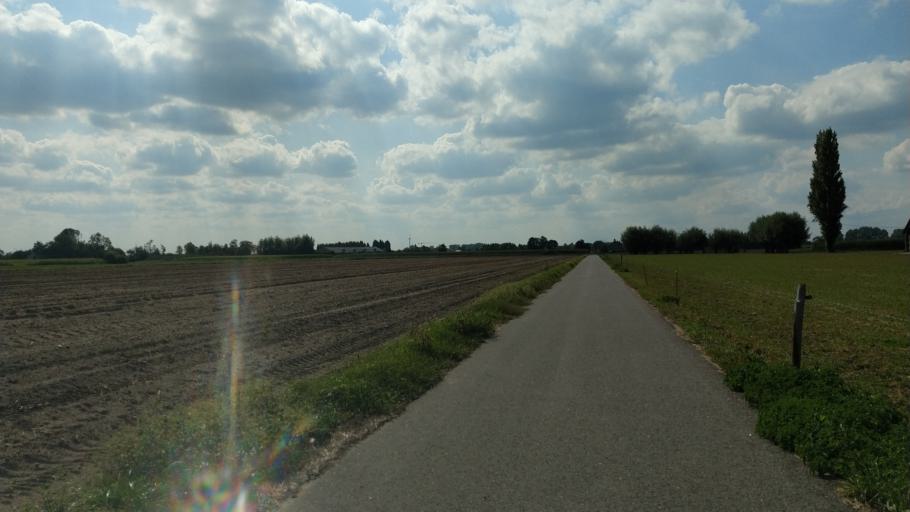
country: BE
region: Flanders
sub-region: Provincie Oost-Vlaanderen
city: Assenede
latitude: 51.2452
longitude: 3.6963
